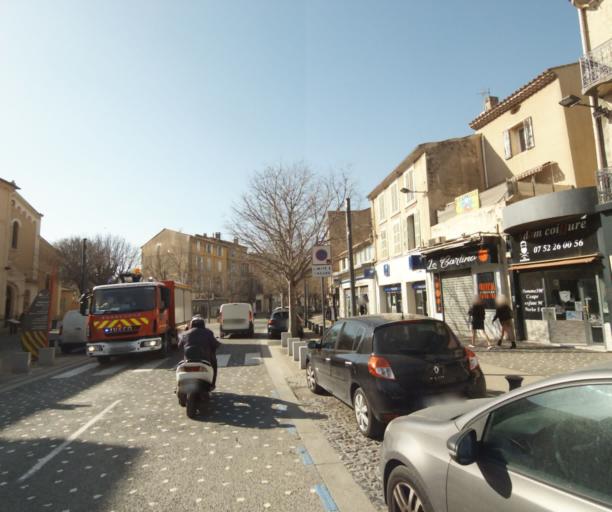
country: FR
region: Provence-Alpes-Cote d'Azur
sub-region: Departement des Bouches-du-Rhone
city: Gardanne
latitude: 43.4541
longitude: 5.4694
